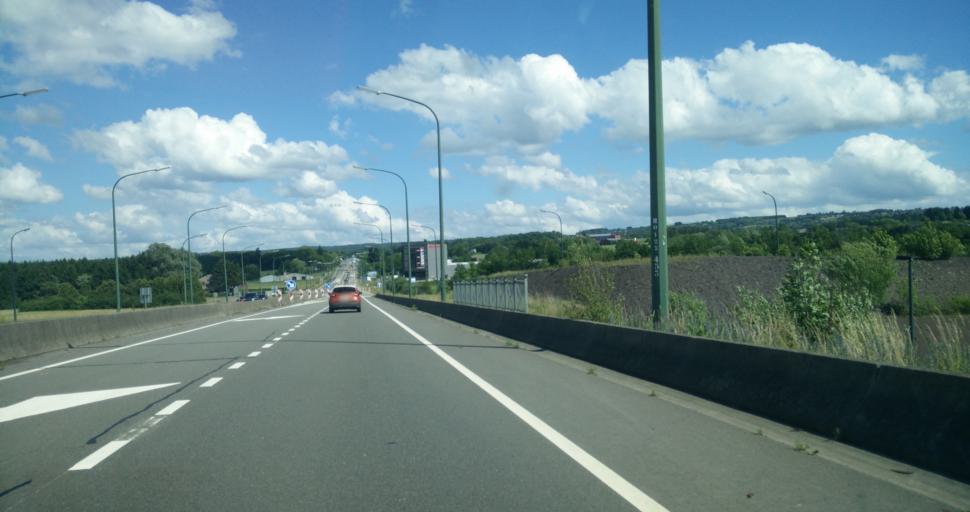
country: BE
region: Wallonia
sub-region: Province du Luxembourg
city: Marche-en-Famenne
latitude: 50.2338
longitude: 5.3089
